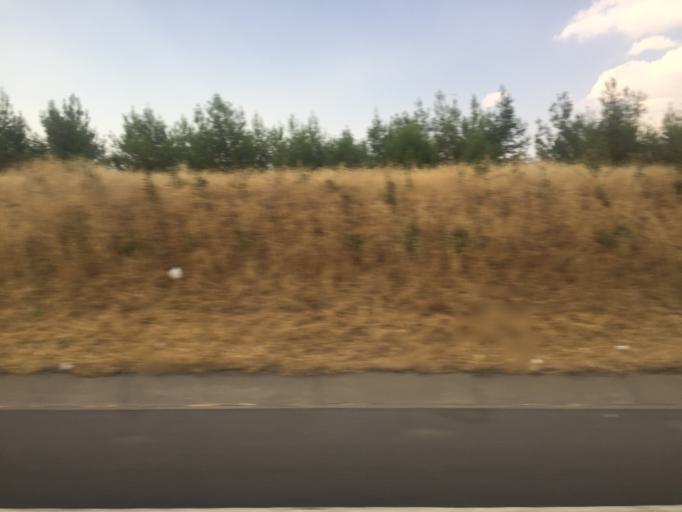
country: TR
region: Sanliurfa
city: Akziyaret
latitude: 37.2678
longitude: 38.7846
